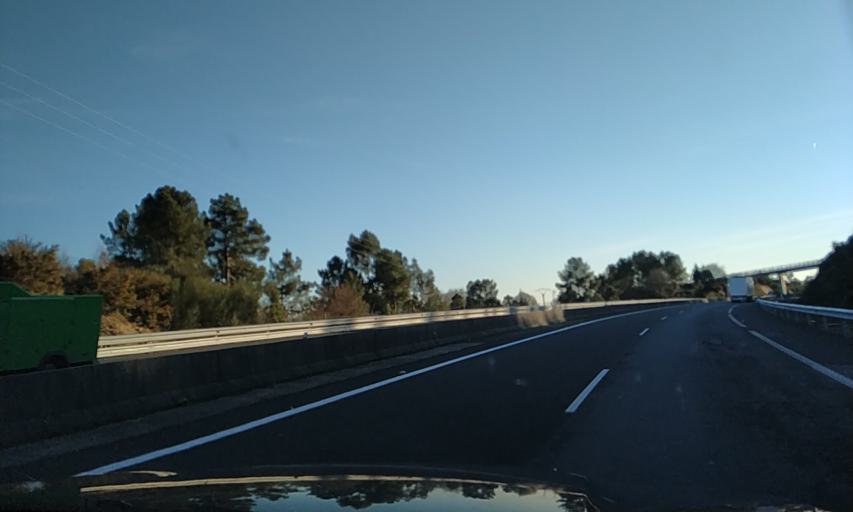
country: ES
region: Galicia
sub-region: Provincia de Ourense
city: Pinor
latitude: 42.5060
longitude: -8.0237
